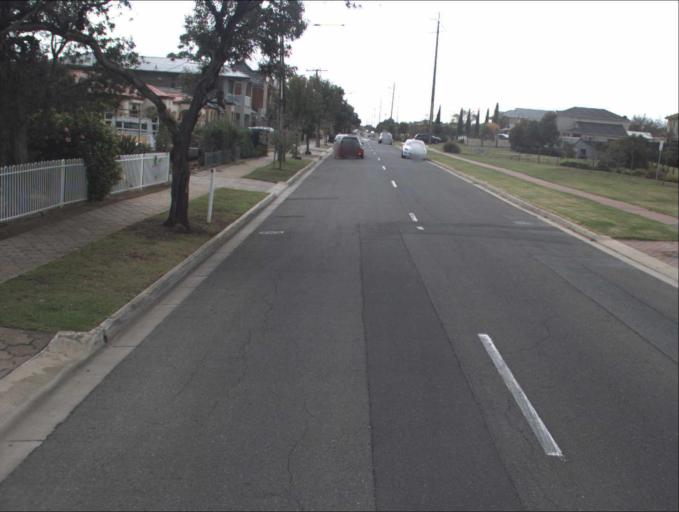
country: AU
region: South Australia
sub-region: Port Adelaide Enfield
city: Klemzig
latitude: -34.8578
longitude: 138.6270
